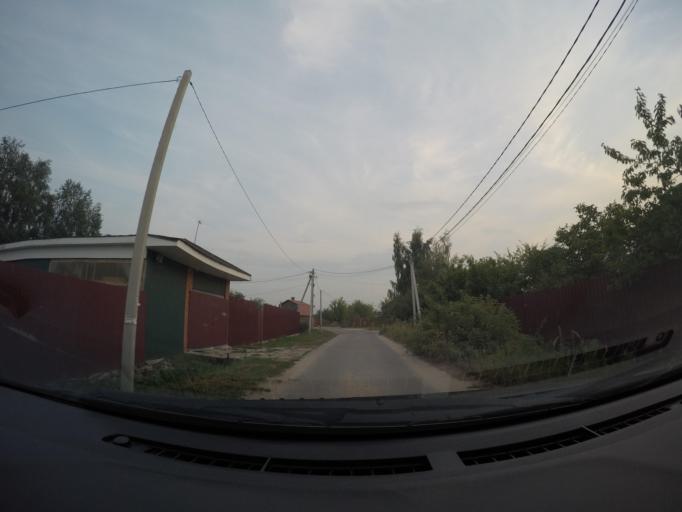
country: RU
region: Moskovskaya
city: Imeni Tsyurupy
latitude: 55.4972
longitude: 38.6592
